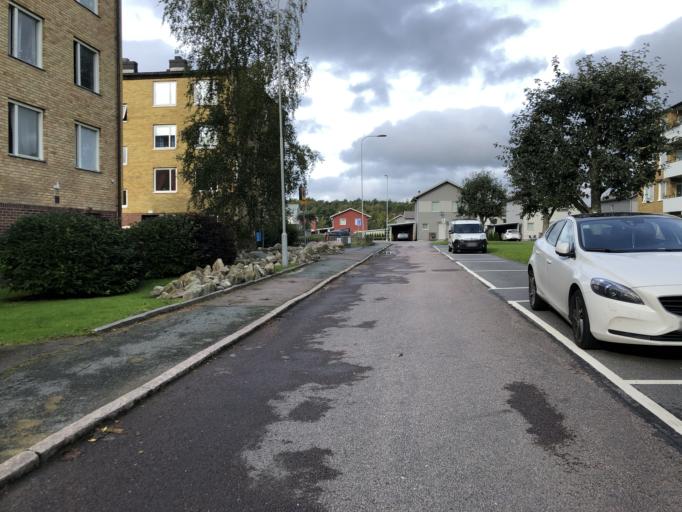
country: SE
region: Vaestra Goetaland
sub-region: Goteborg
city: Majorna
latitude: 57.7344
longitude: 11.8895
